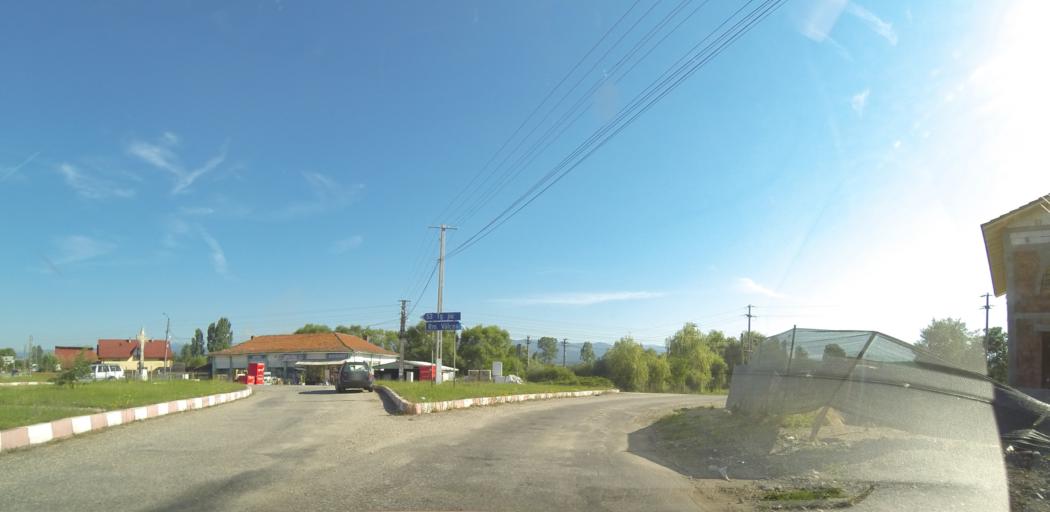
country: RO
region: Gorj
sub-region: Comuna Alimpesti
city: Alimpesti
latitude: 45.1251
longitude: 23.8344
